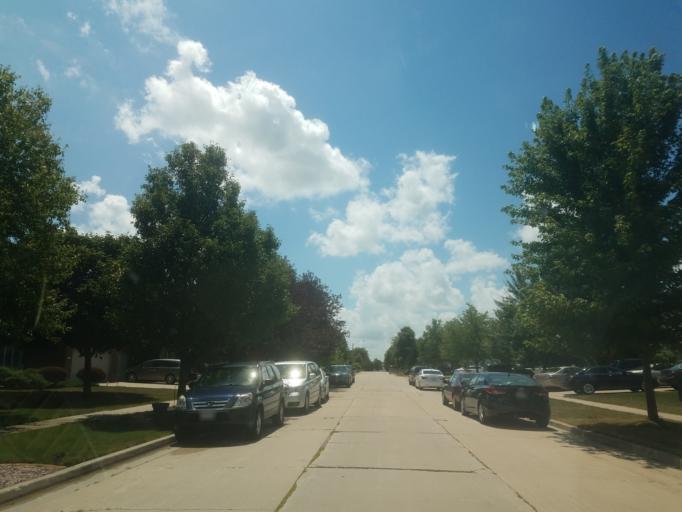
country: US
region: Illinois
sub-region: McLean County
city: Normal
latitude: 40.4985
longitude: -88.9139
